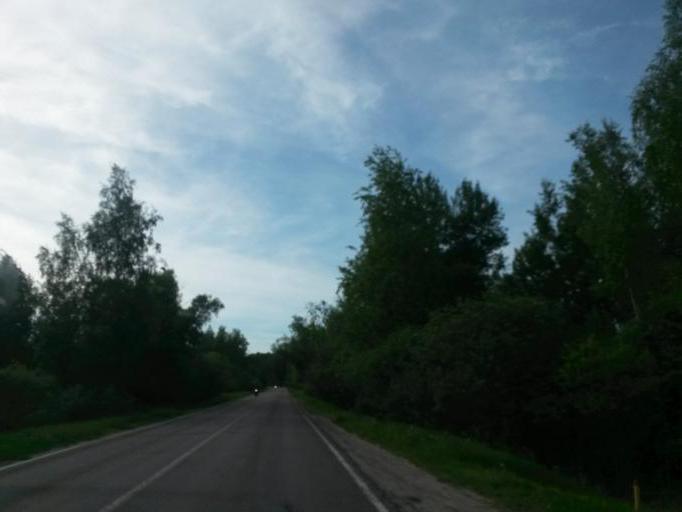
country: RU
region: Moskovskaya
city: Melikhovo
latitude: 55.2171
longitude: 37.6817
